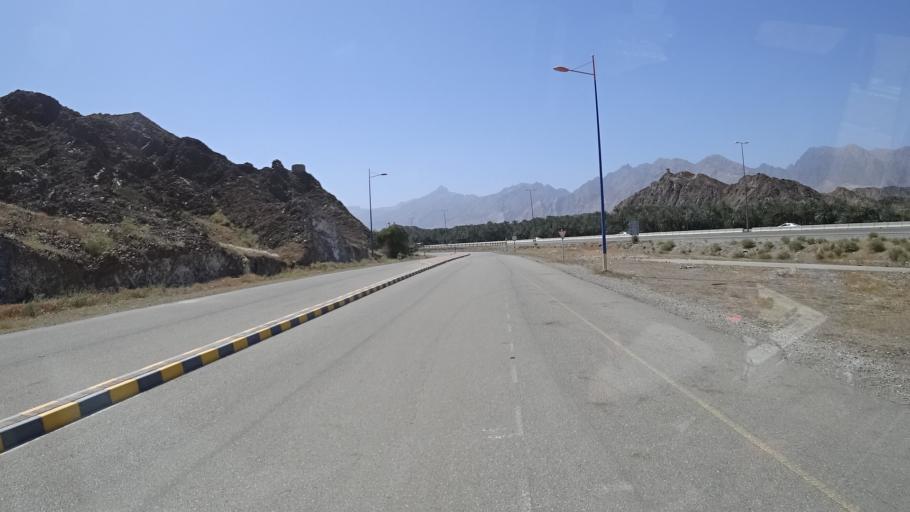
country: OM
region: Muhafazat ad Dakhiliyah
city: Sufalat Sama'il
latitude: 23.3528
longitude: 58.0245
